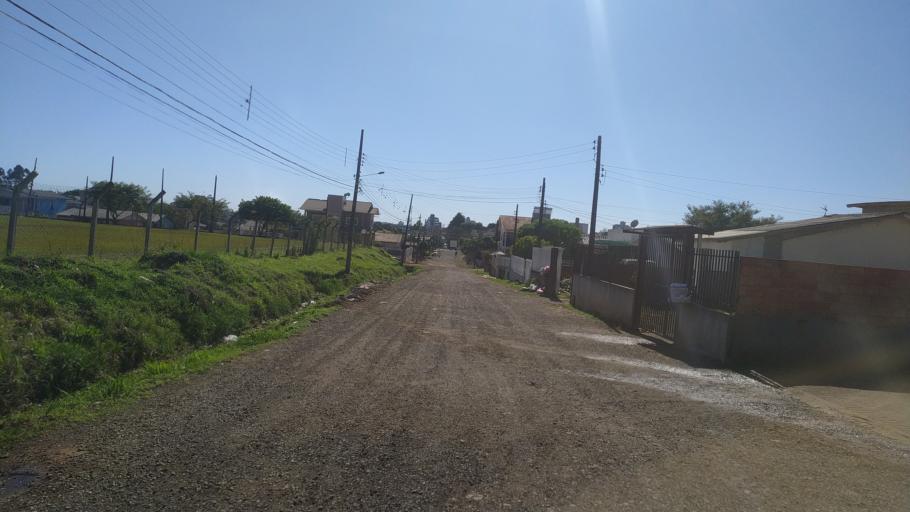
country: BR
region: Santa Catarina
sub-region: Chapeco
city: Chapeco
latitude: -27.1180
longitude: -52.6275
